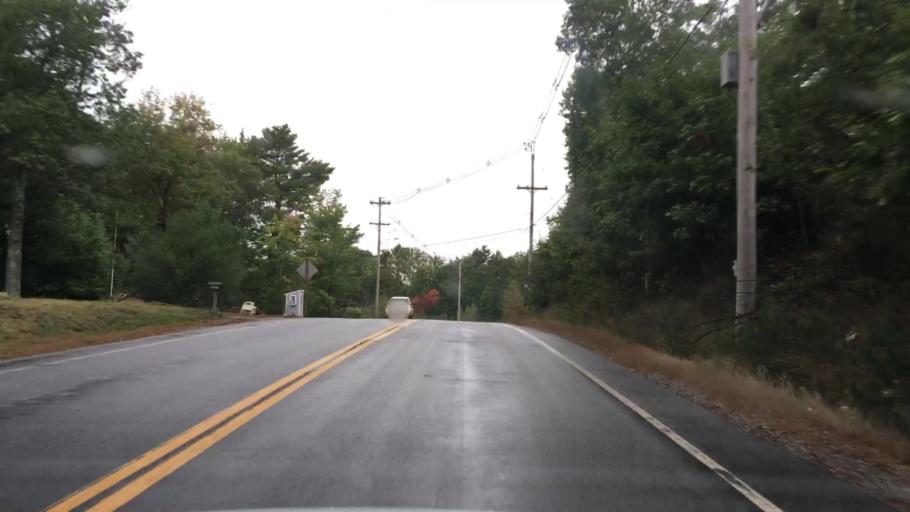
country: US
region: Maine
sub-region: Cumberland County
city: Raymond
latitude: 43.9794
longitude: -70.5268
